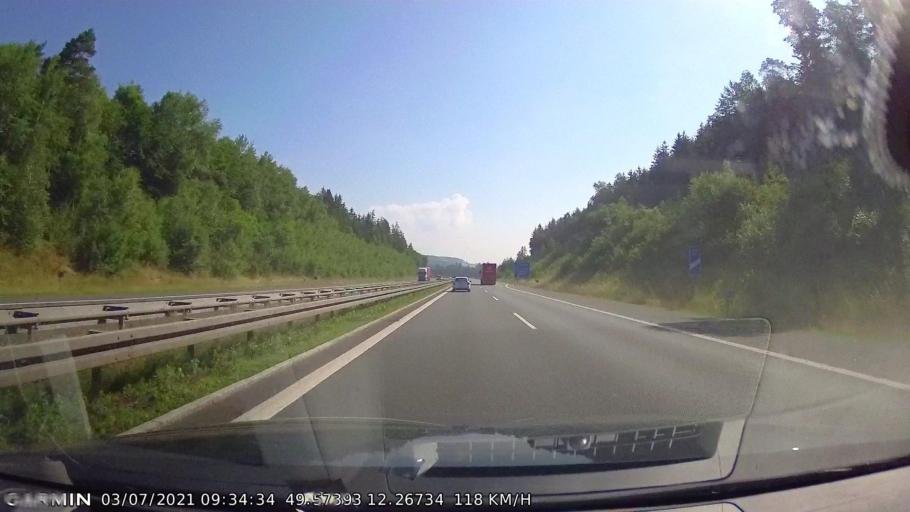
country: DE
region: Bavaria
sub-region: Upper Palatinate
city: Leuchtenberg
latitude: 49.5739
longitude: 12.2674
